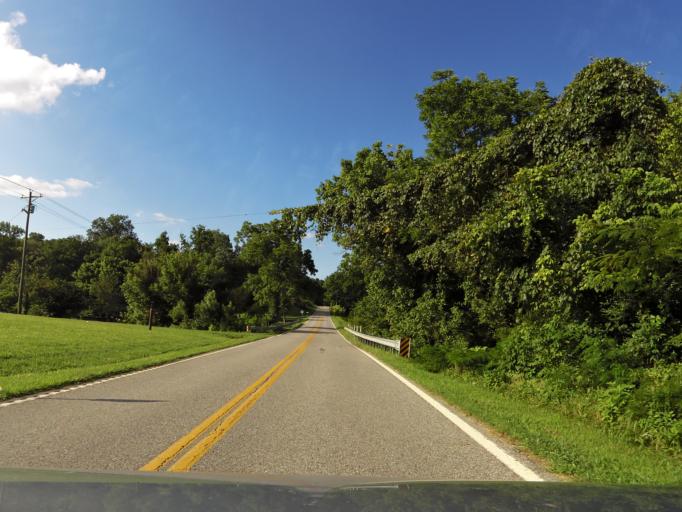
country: US
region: Tennessee
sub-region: Blount County
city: Maryville
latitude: 35.6240
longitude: -84.0255
